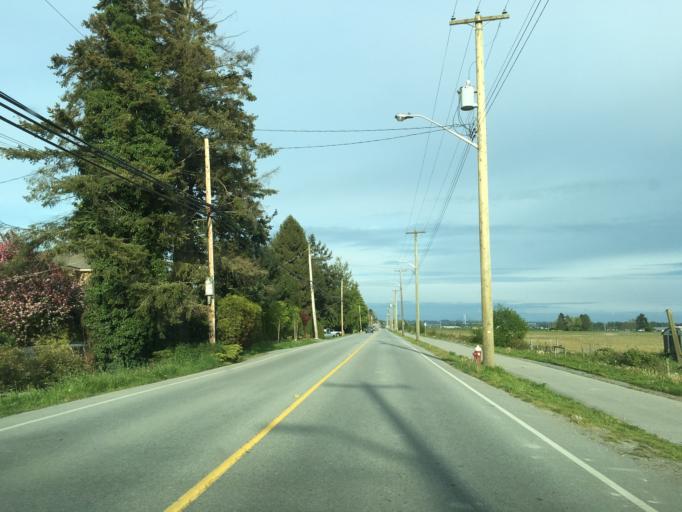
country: CA
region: British Columbia
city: Ladner
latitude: 49.1699
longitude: -123.0342
